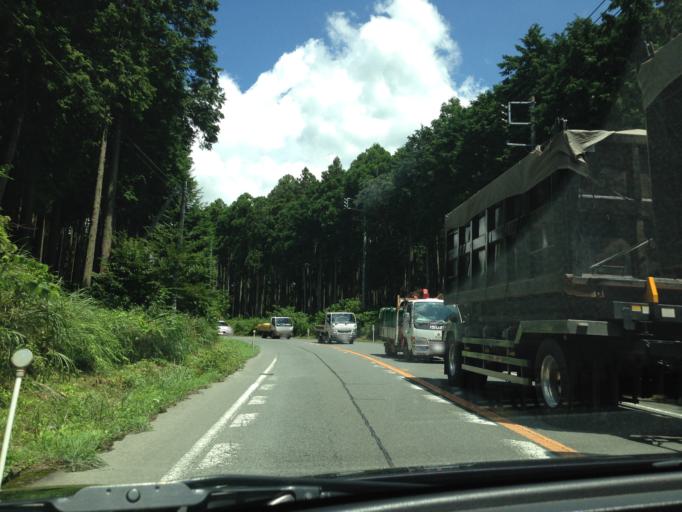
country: JP
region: Shizuoka
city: Fuji
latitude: 35.2154
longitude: 138.7303
